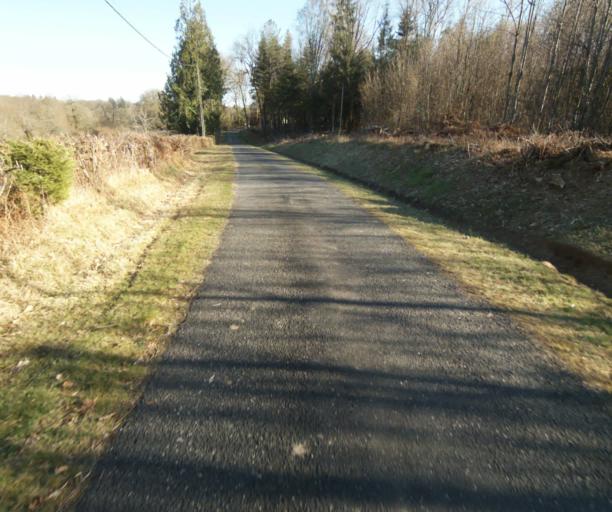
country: FR
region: Limousin
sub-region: Departement de la Correze
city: Seilhac
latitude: 45.3864
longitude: 1.6983
